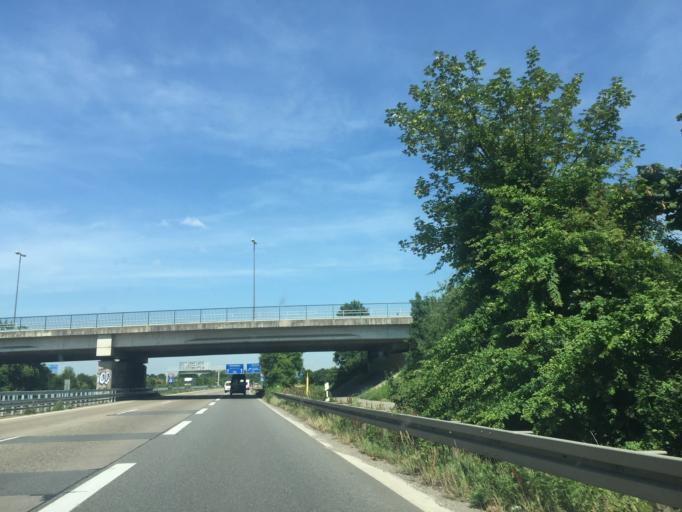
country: DE
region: Baden-Wuerttemberg
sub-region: Karlsruhe Region
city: Eppelheim
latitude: 49.4140
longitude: 8.6440
